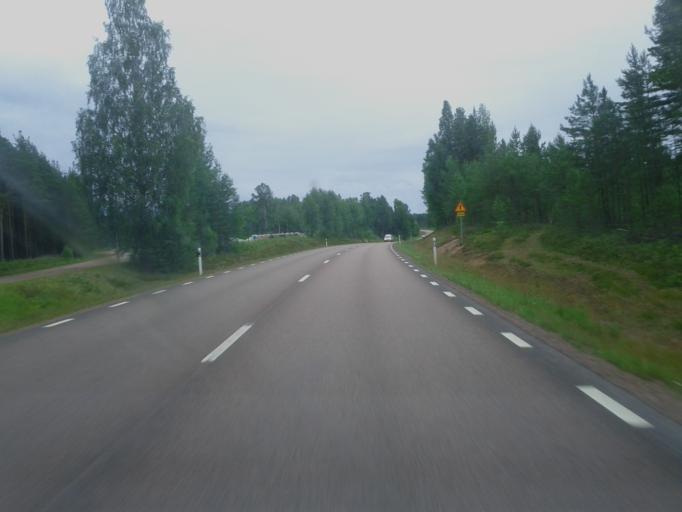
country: SE
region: Dalarna
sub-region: Mora Kommun
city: Mora
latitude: 61.0409
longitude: 14.5051
